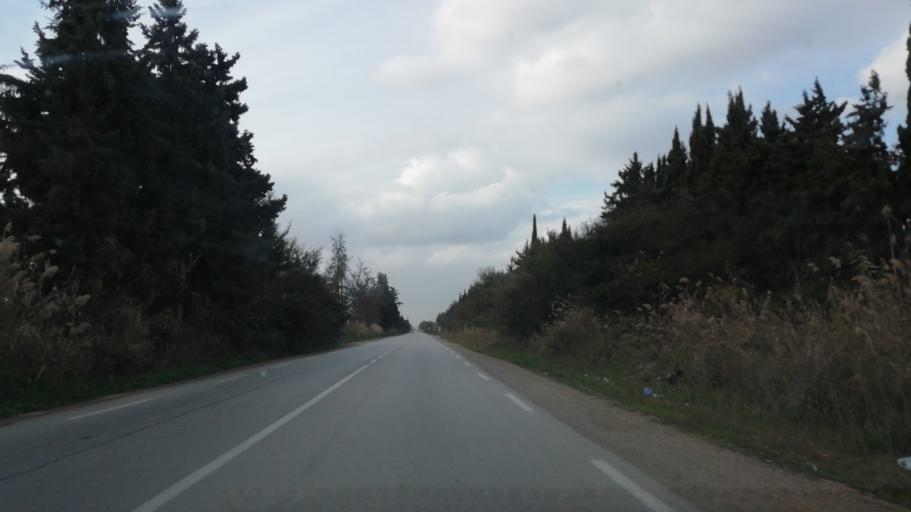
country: DZ
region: Mascara
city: Sig
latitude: 35.6676
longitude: -0.0005
